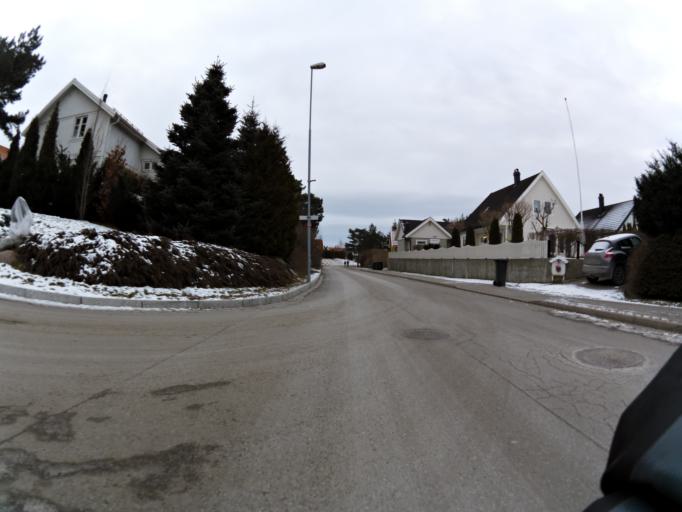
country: NO
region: Ostfold
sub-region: Fredrikstad
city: Fredrikstad
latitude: 59.1951
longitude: 10.8723
